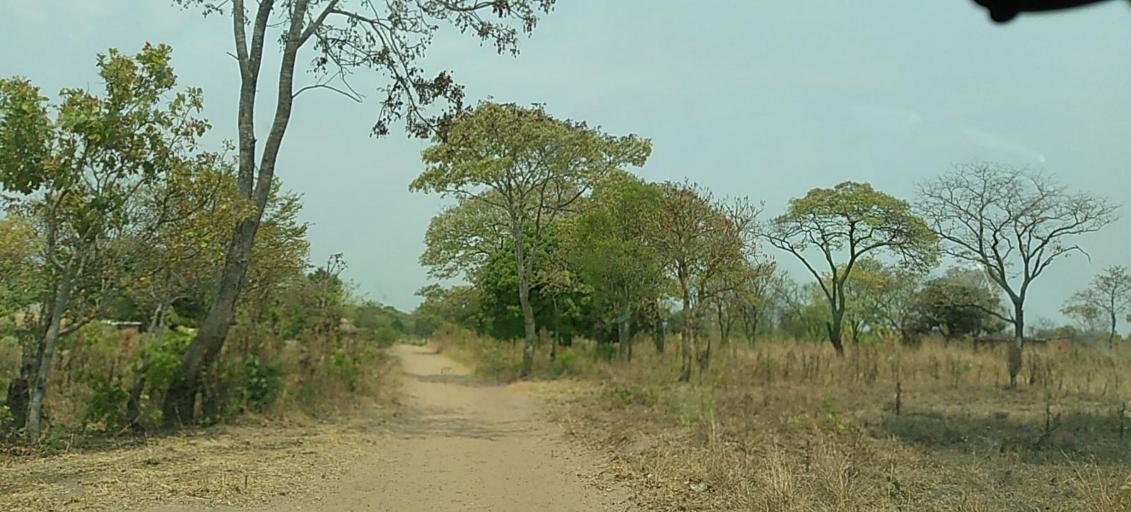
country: ZM
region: North-Western
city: Kabompo
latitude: -13.5338
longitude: 24.4592
